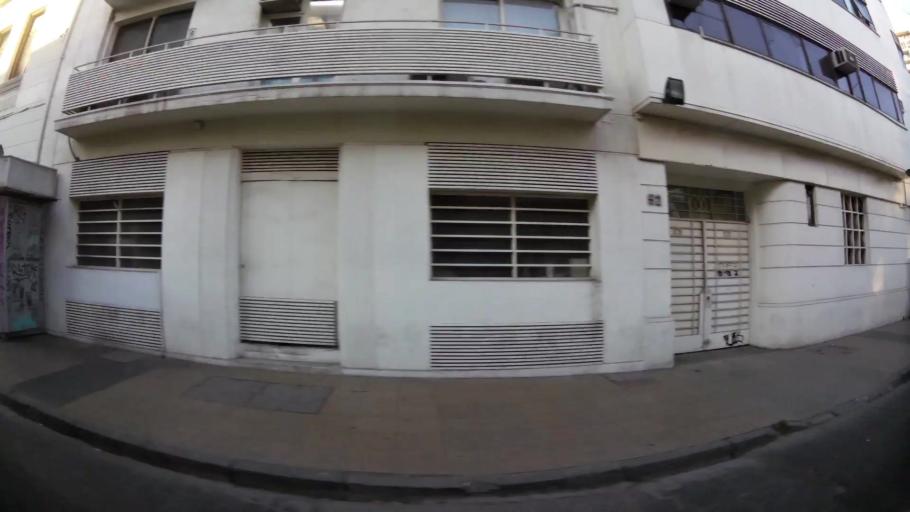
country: CL
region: Santiago Metropolitan
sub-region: Provincia de Santiago
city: Santiago
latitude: -33.4427
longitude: -70.6412
